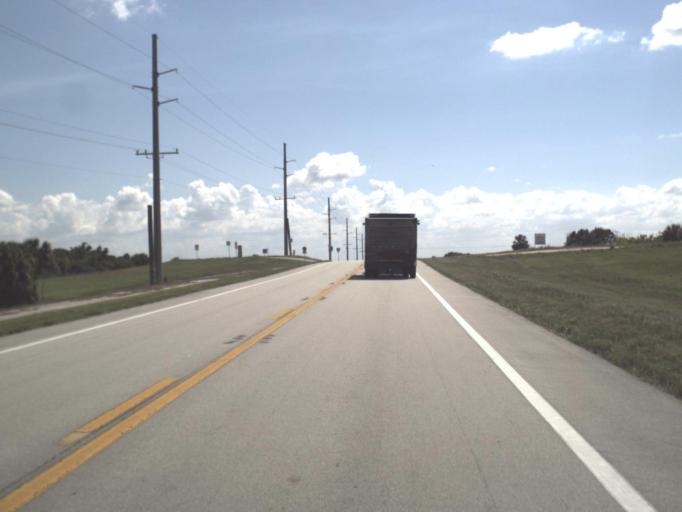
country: US
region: Florida
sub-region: Glades County
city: Moore Haven
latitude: 26.9261
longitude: -81.1223
